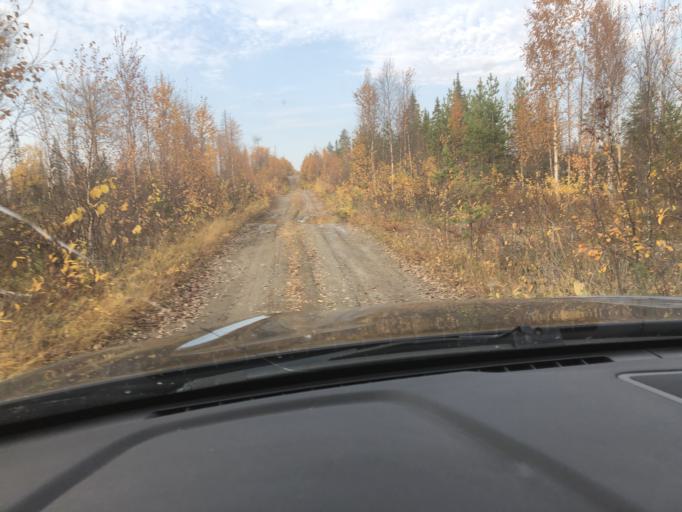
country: FI
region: Northern Ostrobothnia
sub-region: Koillismaa
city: Kuusamo
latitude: 66.4819
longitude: 29.4445
